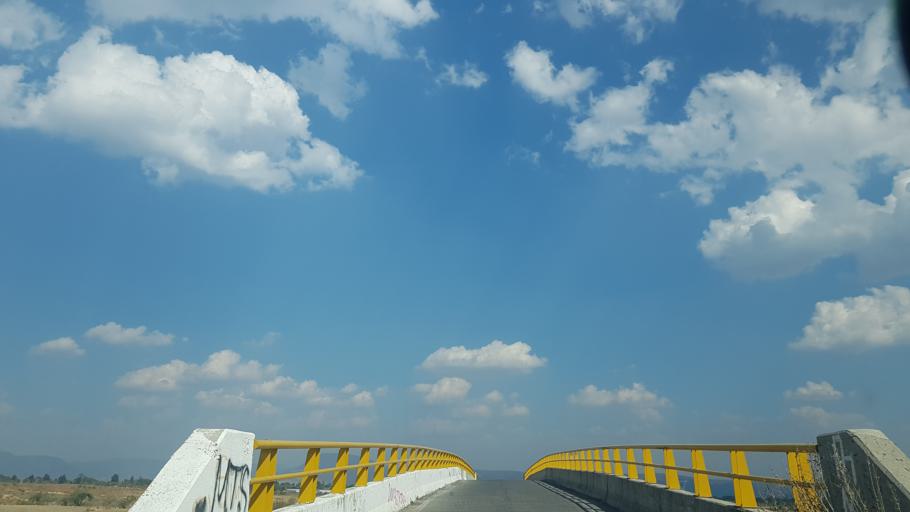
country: MX
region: Puebla
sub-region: Atlixco
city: Colonia Agricola de Ocotepec (Colonia San Jose)
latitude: 18.8873
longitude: -98.4990
